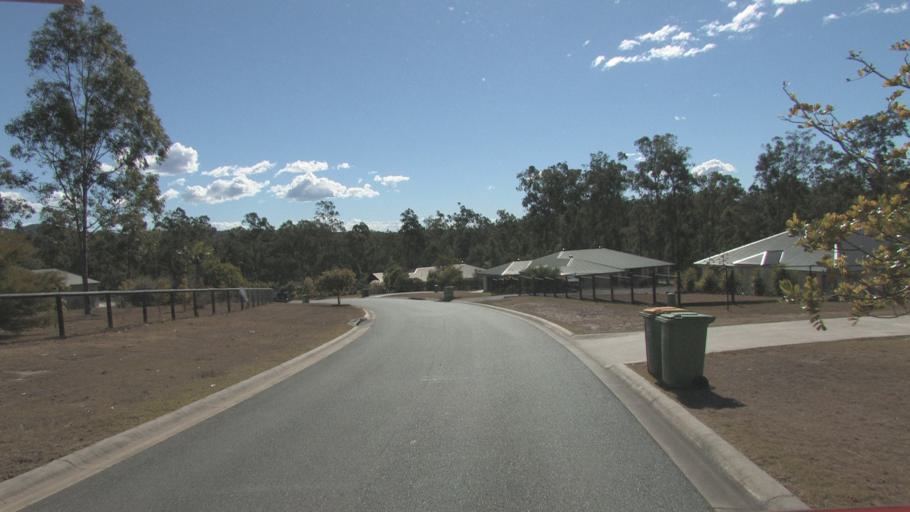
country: AU
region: Queensland
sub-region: Logan
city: North Maclean
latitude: -27.7515
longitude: 152.9346
